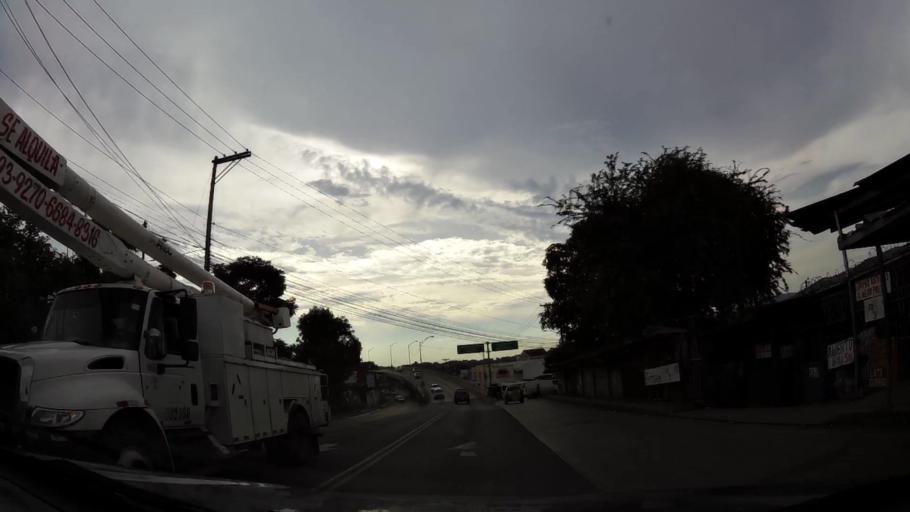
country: PA
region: Panama
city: Tocumen
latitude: 9.1038
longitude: -79.3643
